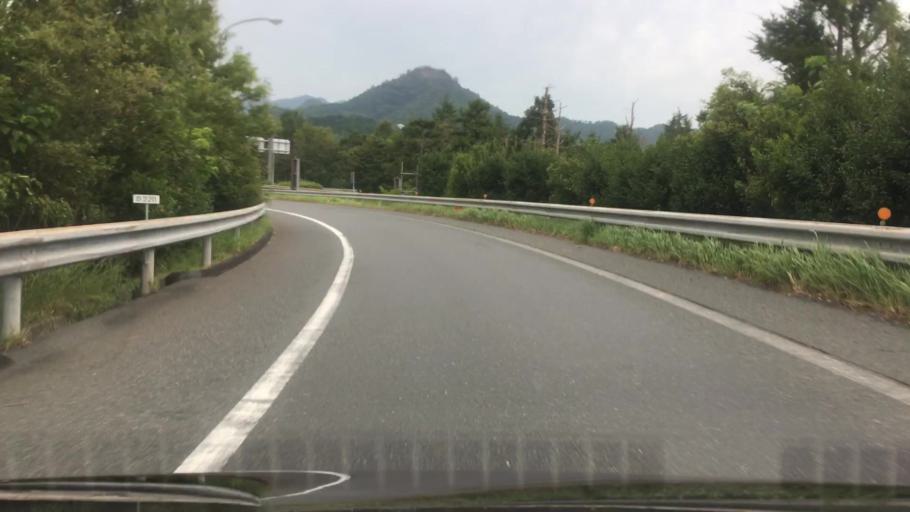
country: JP
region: Kyoto
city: Fukuchiyama
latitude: 35.1638
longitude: 135.1186
